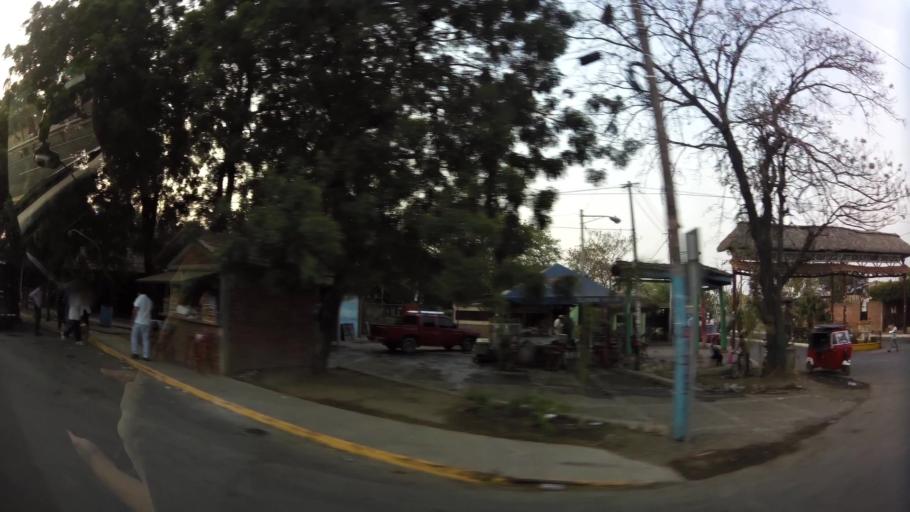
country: NI
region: Leon
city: La Paz Centro
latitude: 12.3349
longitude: -86.6765
